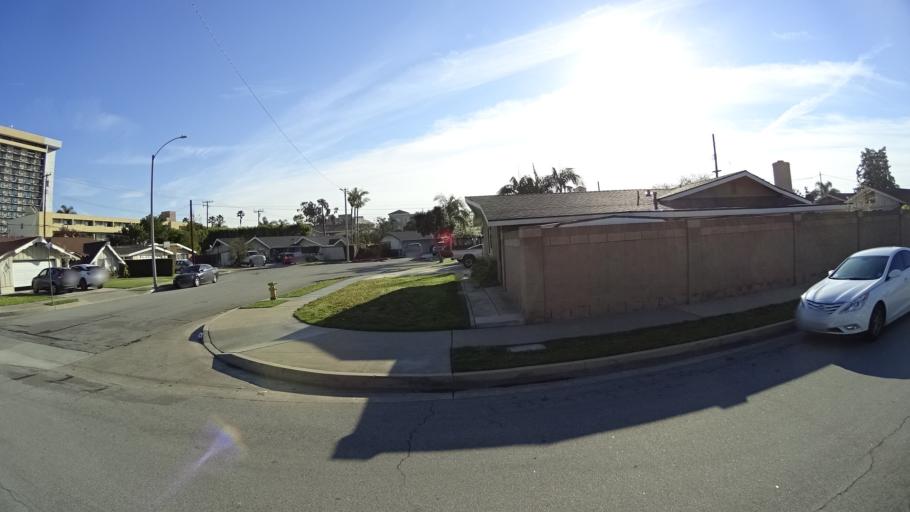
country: US
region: California
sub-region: Orange County
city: Garden Grove
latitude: 33.7973
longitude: -117.9192
